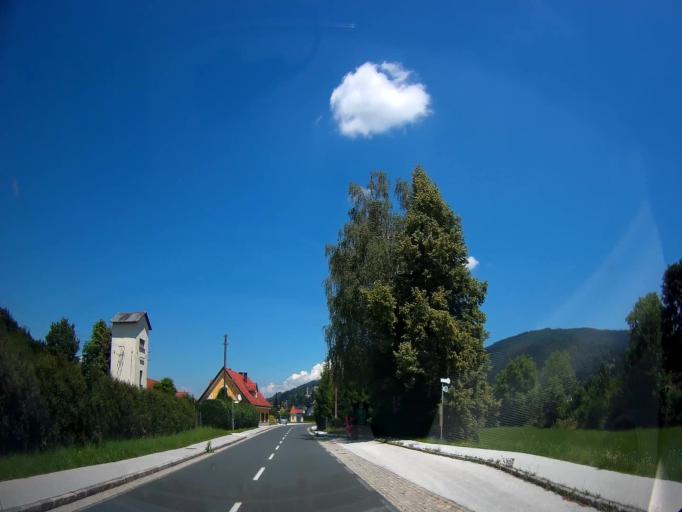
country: AT
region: Carinthia
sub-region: Politischer Bezirk Volkermarkt
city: Bleiburg/Pliberk
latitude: 46.5800
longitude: 14.7940
